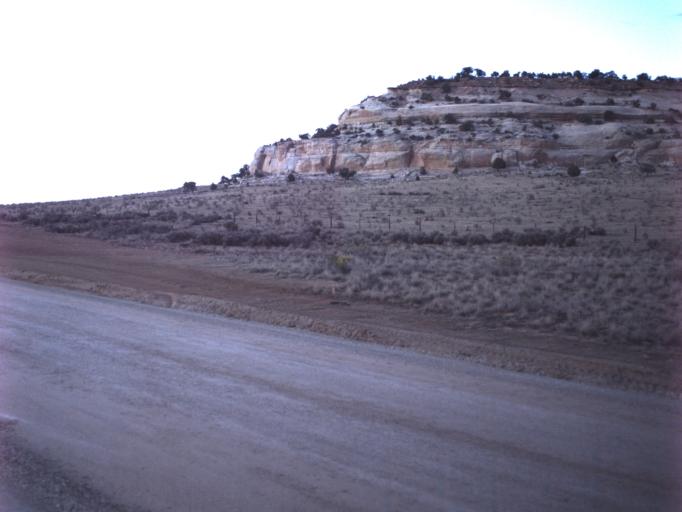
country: US
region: Utah
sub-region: San Juan County
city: Monticello
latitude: 38.0978
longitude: -109.3595
